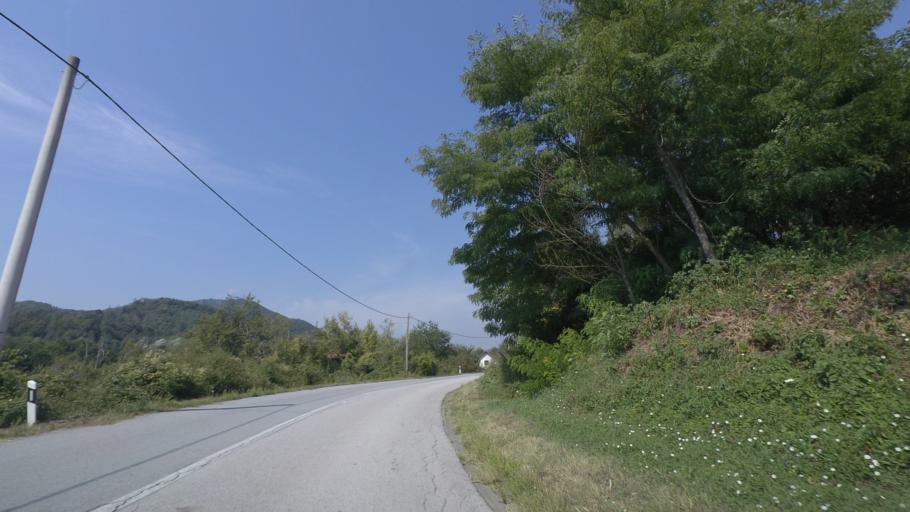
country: BA
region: Federation of Bosnia and Herzegovina
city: Zboriste
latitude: 45.1353
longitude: 16.1820
